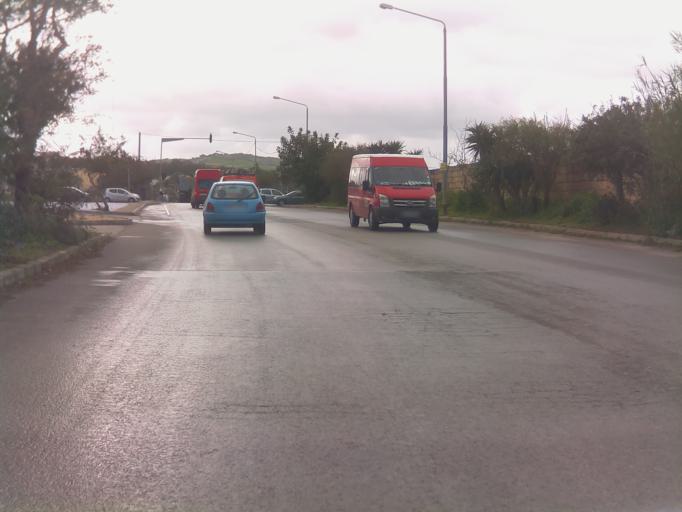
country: MT
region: Il-Mosta
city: Mosta
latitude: 35.9188
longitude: 14.4217
